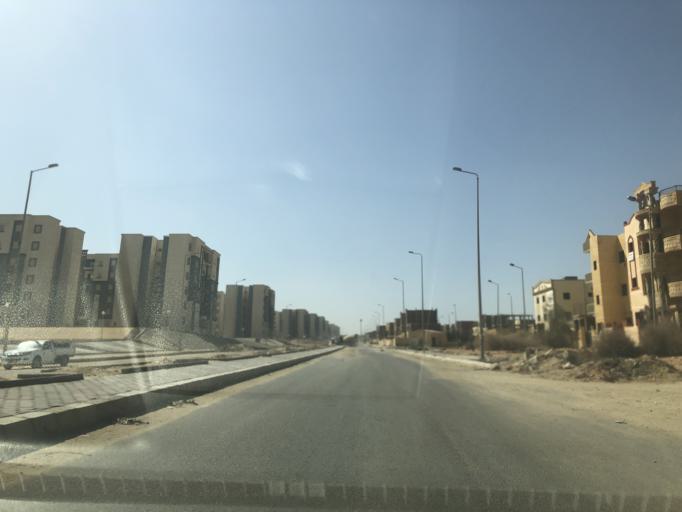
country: EG
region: Al Jizah
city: Madinat Sittah Uktubar
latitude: 29.9304
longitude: 30.9885
